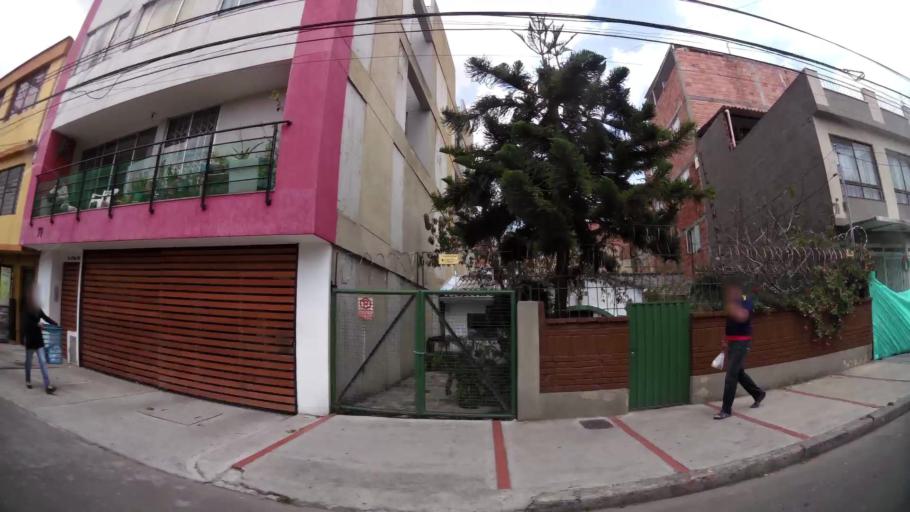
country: CO
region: Cundinamarca
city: La Calera
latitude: 4.7302
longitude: -74.0278
